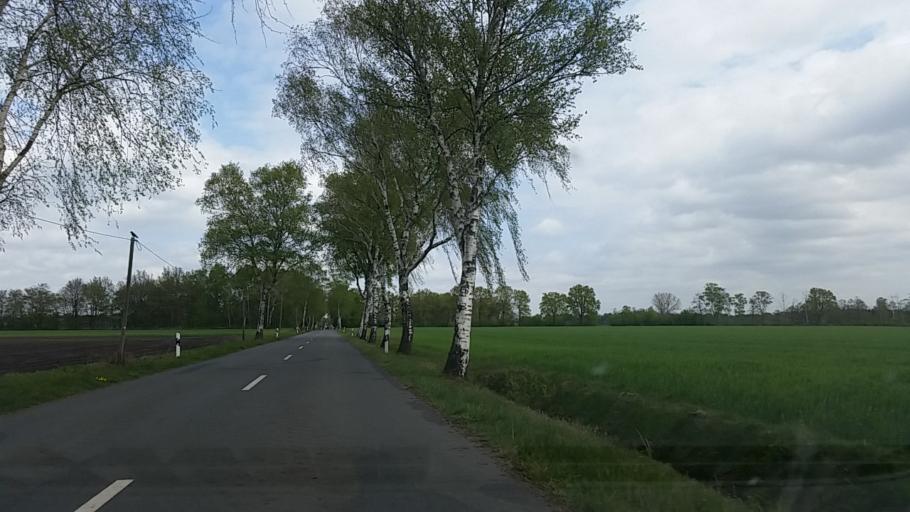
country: DE
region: Lower Saxony
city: Konigsmoor
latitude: 53.2096
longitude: 9.7112
